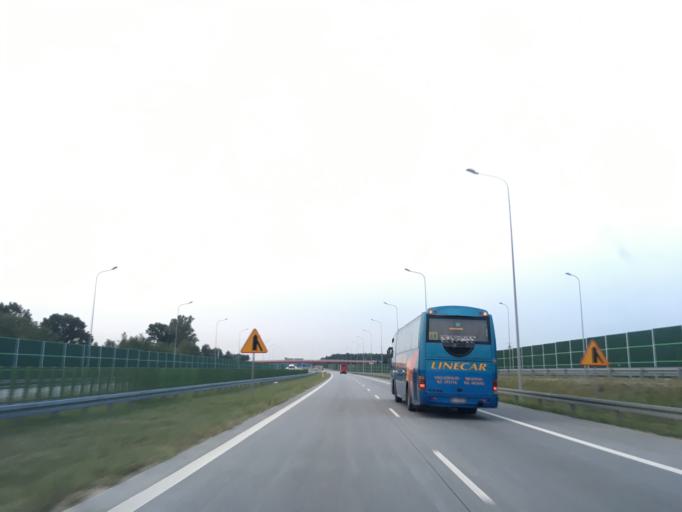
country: PL
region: Lodz Voivodeship
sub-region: Powiat lodzki wschodni
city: Tuszyn
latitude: 51.6361
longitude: 19.5700
